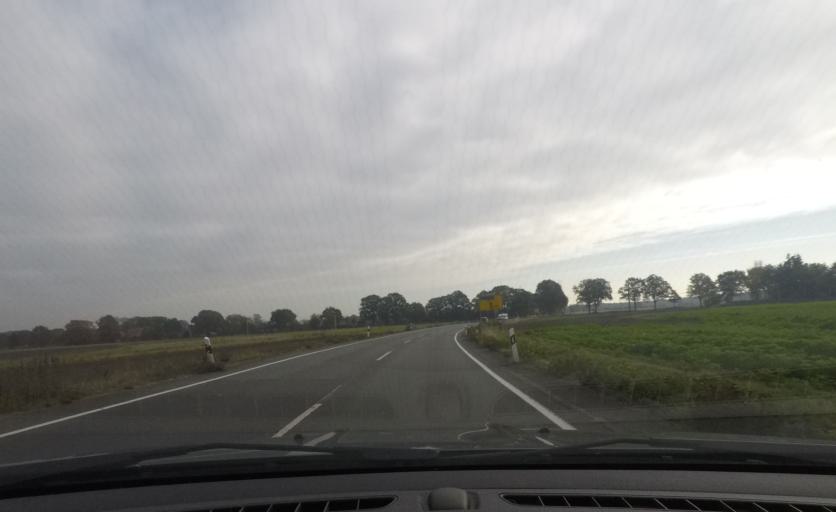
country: DE
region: North Rhine-Westphalia
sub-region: Regierungsbezirk Munster
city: Klein Reken
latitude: 51.8621
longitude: 7.1025
